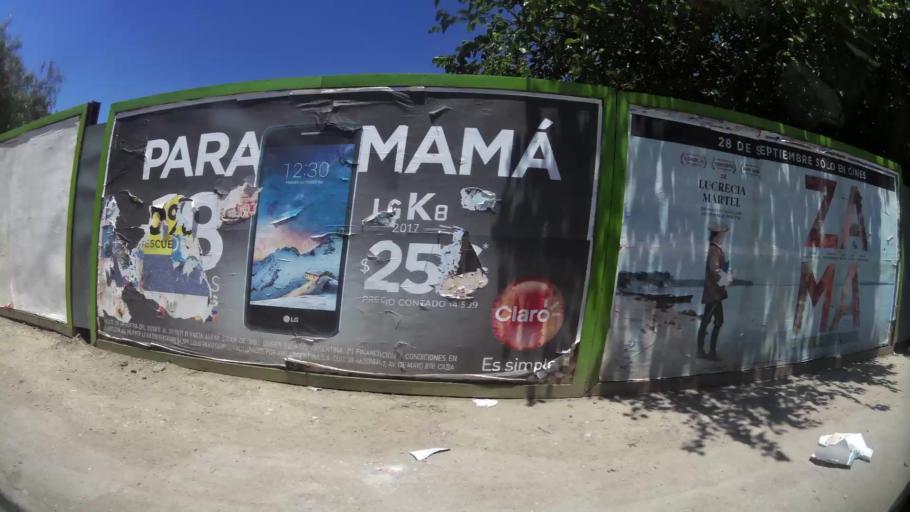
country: AR
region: Cordoba
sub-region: Departamento de Capital
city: Cordoba
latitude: -31.3917
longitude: -64.2088
